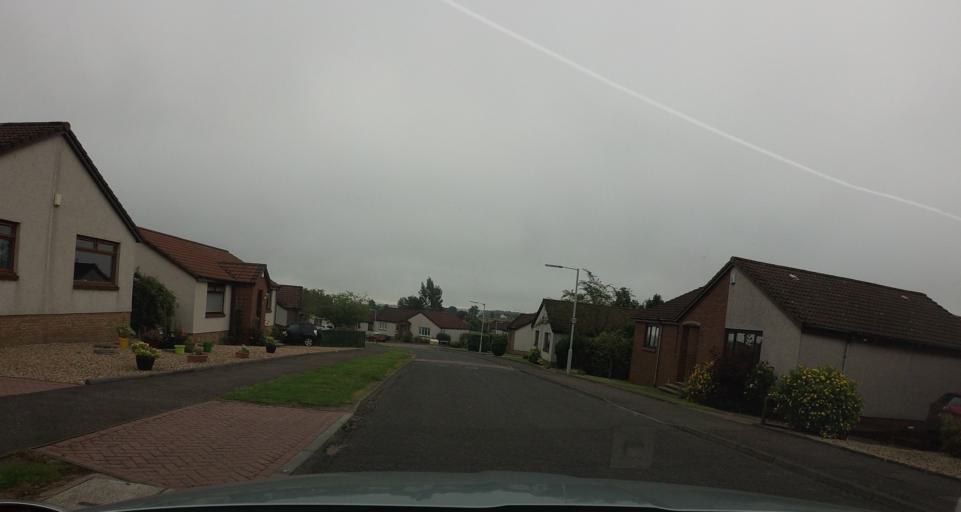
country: GB
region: Scotland
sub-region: Fife
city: Kelty
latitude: 56.1353
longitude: -3.3741
